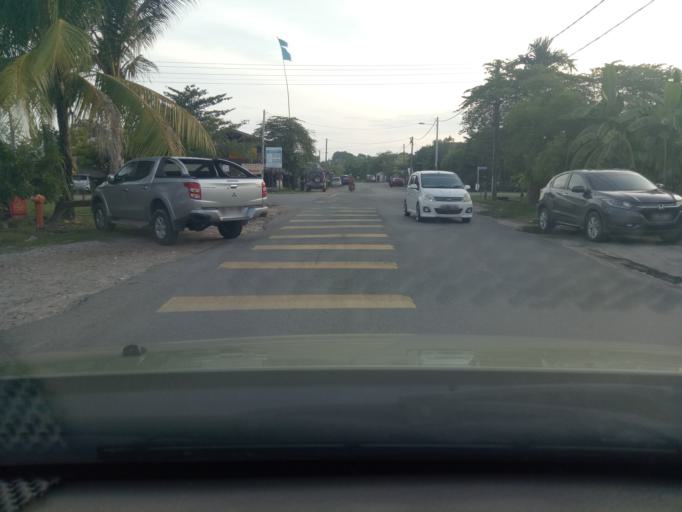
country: MY
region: Kedah
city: Alor Setar
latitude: 6.1225
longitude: 100.3561
